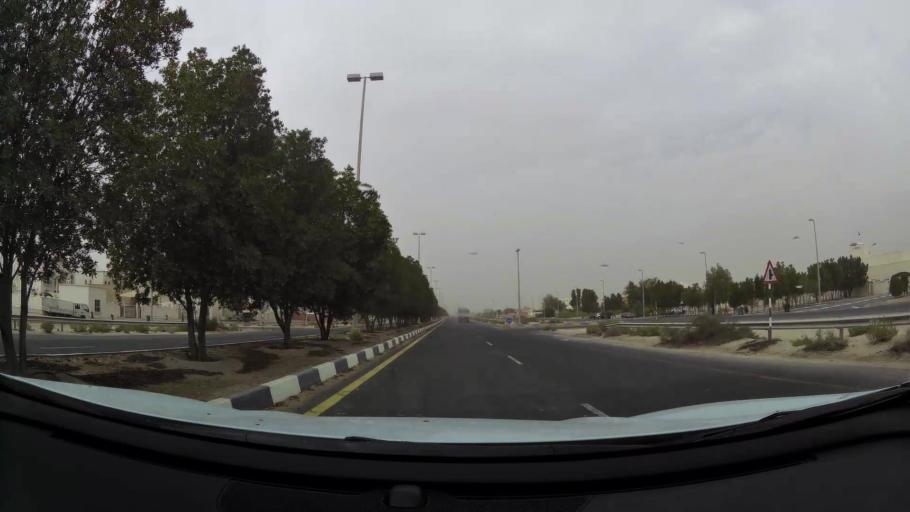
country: AE
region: Abu Dhabi
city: Abu Dhabi
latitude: 24.3630
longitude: 54.7138
